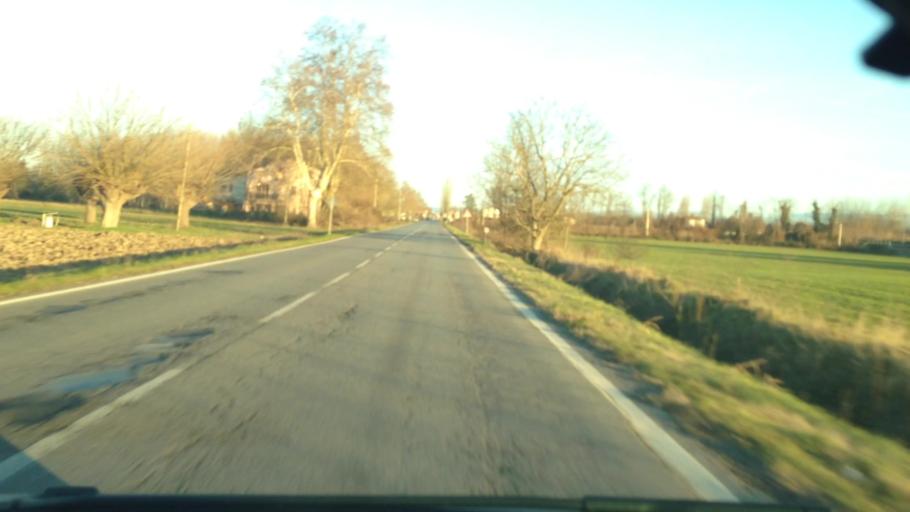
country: IT
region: Piedmont
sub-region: Provincia di Alessandria
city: Solero
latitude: 44.9212
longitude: 8.5388
